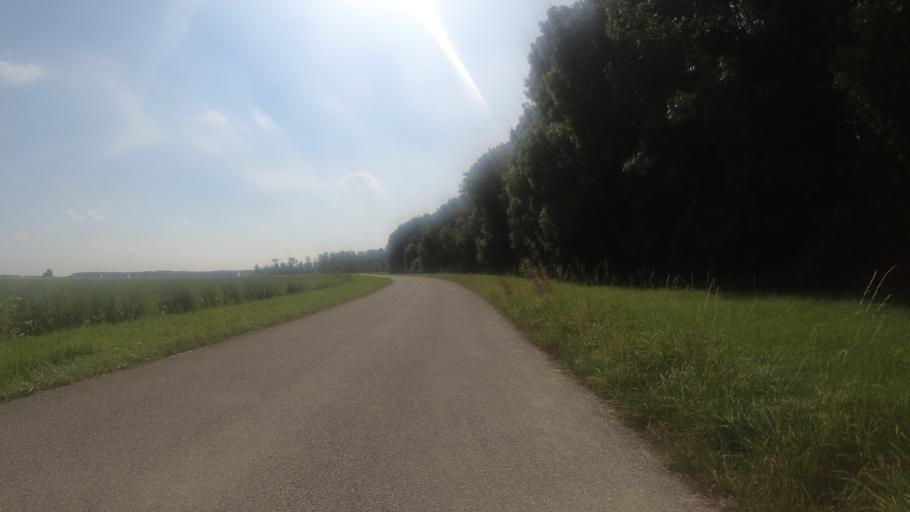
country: NL
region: Zeeland
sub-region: Gemeente Noord-Beveland
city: Kamperland
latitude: 51.5378
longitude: 3.7070
